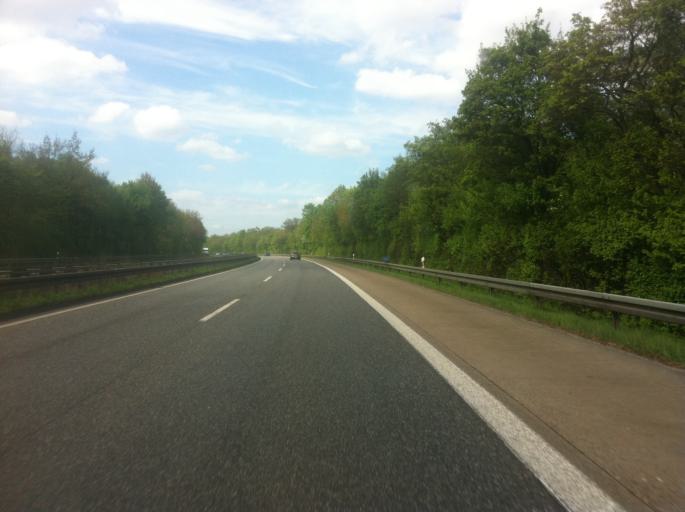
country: DE
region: North Rhine-Westphalia
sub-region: Regierungsbezirk Koln
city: Wachtberg
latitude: 50.6690
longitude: 7.0613
